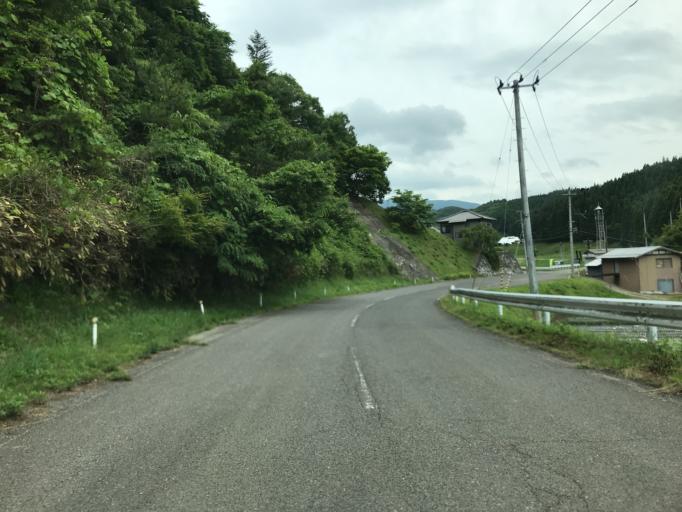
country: JP
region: Fukushima
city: Funehikimachi-funehiki
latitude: 37.4002
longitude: 140.6629
